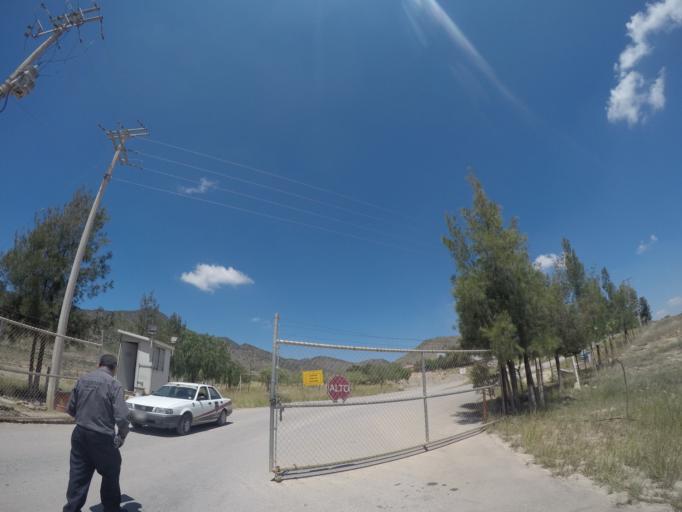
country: MX
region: San Luis Potosi
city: La Pila
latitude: 22.0160
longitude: -100.9156
